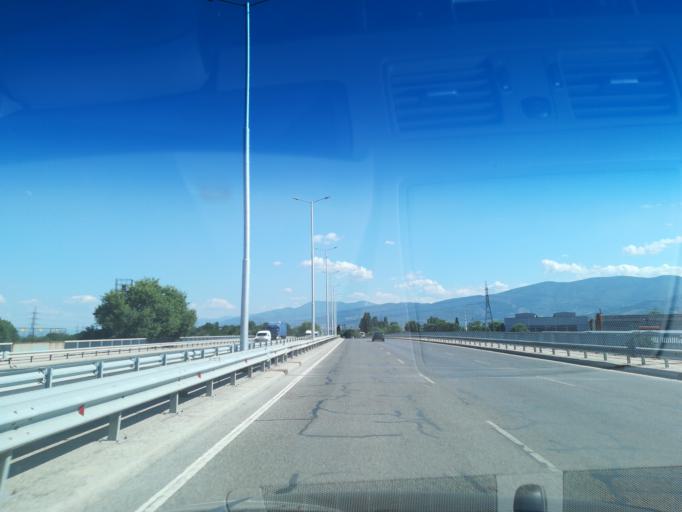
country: BG
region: Plovdiv
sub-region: Obshtina Plovdiv
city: Plovdiv
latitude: 42.1169
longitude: 24.7767
